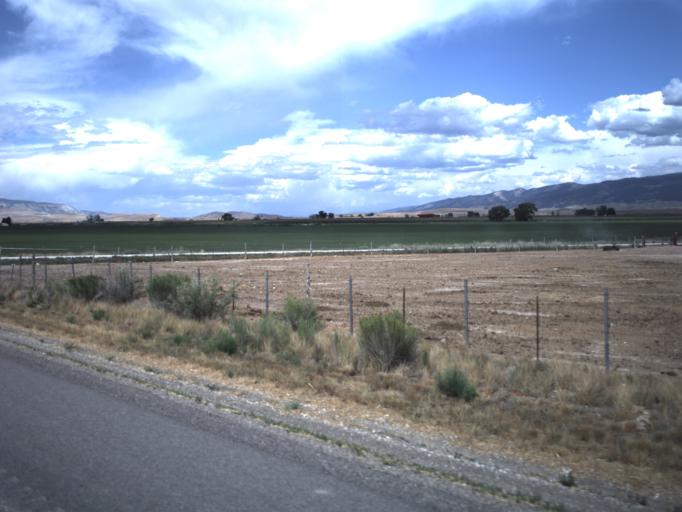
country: US
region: Utah
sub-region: Sanpete County
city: Centerfield
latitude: 39.0725
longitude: -111.8209
